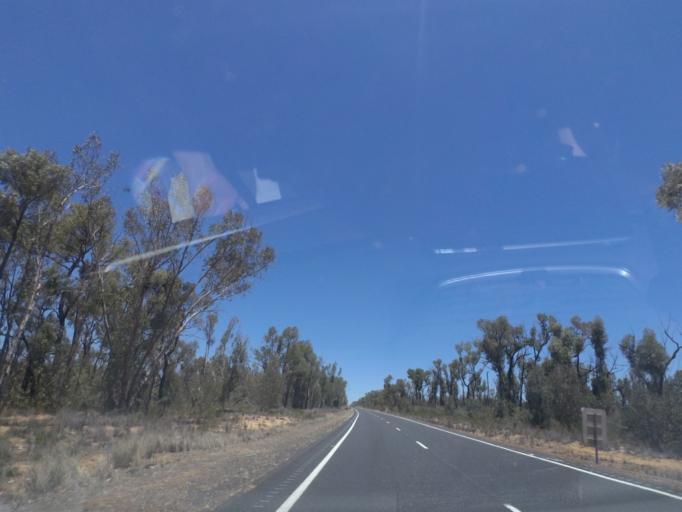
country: AU
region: New South Wales
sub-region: Warrumbungle Shire
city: Coonabarabran
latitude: -30.9456
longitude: 149.4223
